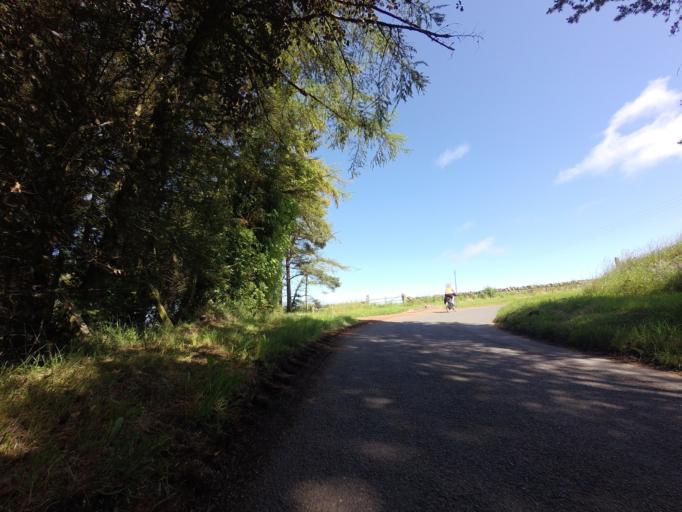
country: GB
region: Scotland
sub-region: Aberdeenshire
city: Banff
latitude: 57.6177
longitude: -2.5088
